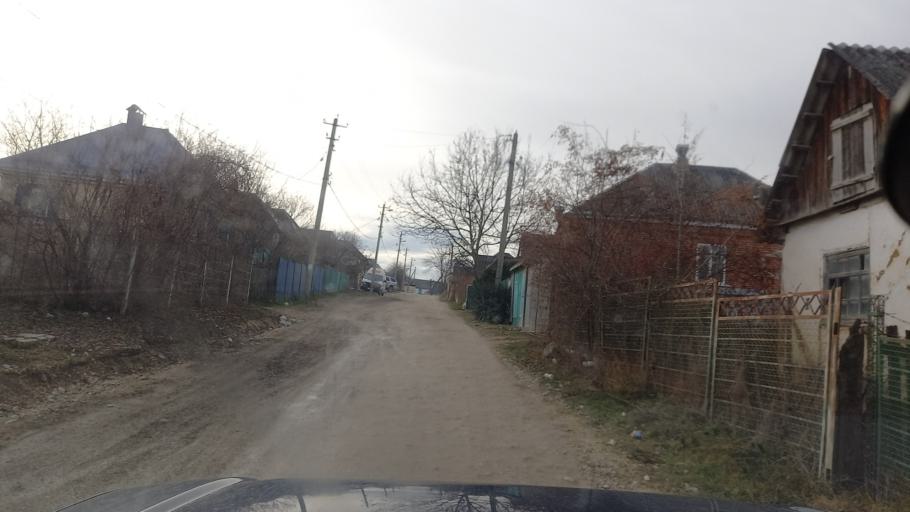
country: RU
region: Adygeya
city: Kamennomostskiy
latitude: 44.2940
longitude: 40.1906
